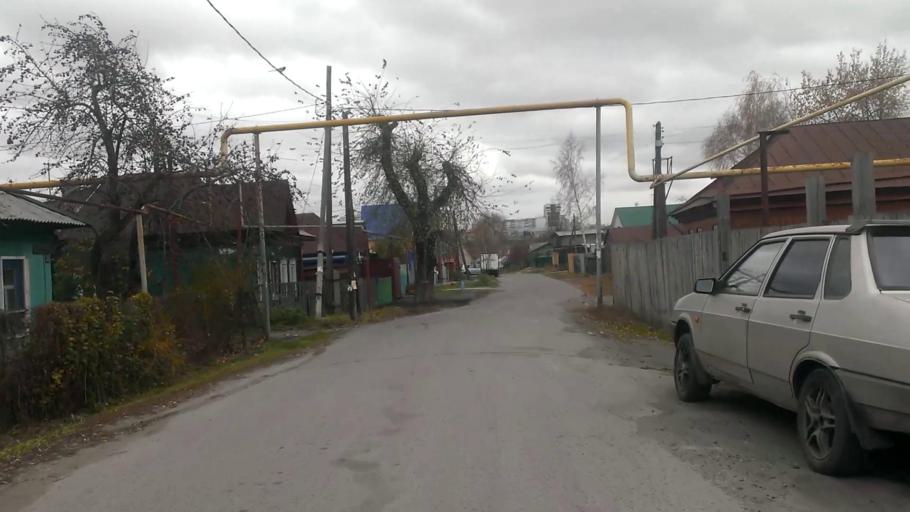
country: RU
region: Altai Krai
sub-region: Gorod Barnaulskiy
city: Barnaul
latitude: 53.3519
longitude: 83.7467
